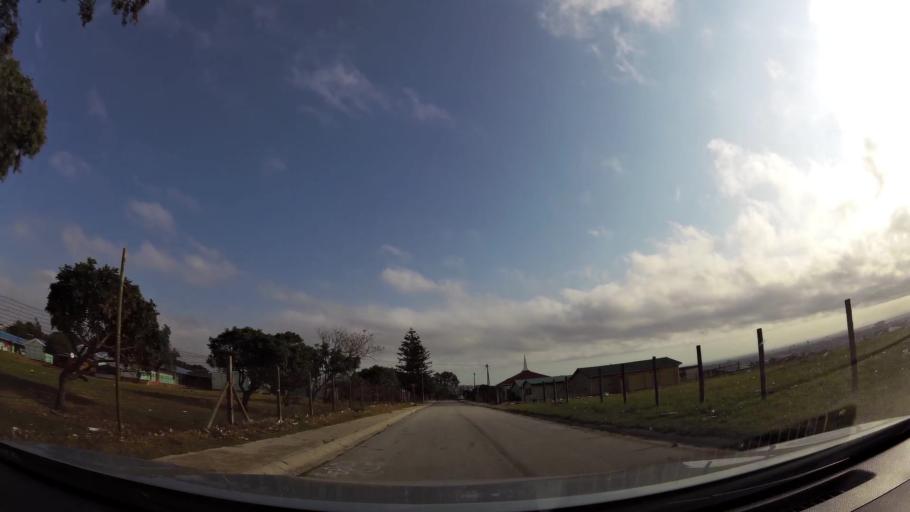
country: ZA
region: Eastern Cape
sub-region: Nelson Mandela Bay Metropolitan Municipality
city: Port Elizabeth
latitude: -33.9260
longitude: 25.5572
